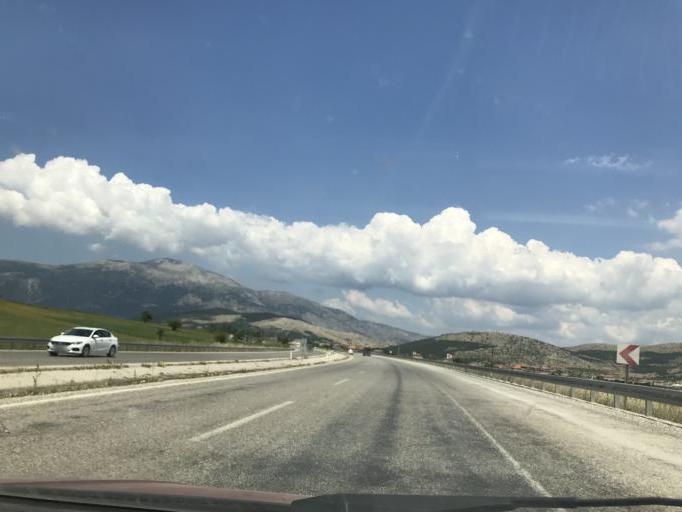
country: TR
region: Denizli
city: Serinhisar
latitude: 37.6165
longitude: 29.1820
